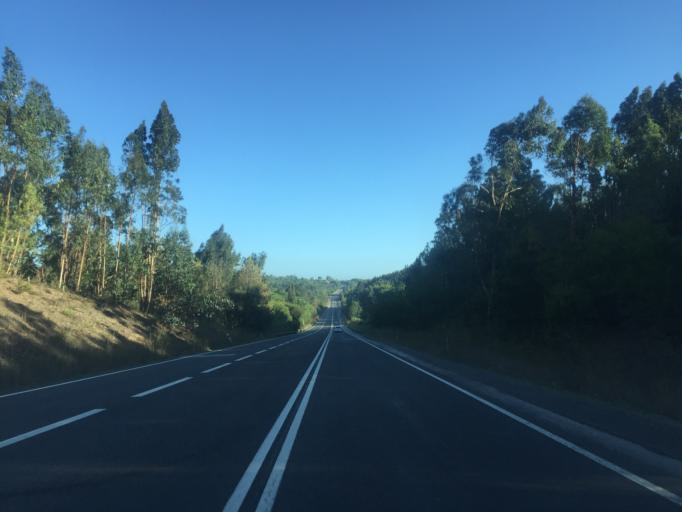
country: PT
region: Lisbon
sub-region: Azambuja
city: Alcoentre
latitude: 39.2606
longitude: -8.9506
